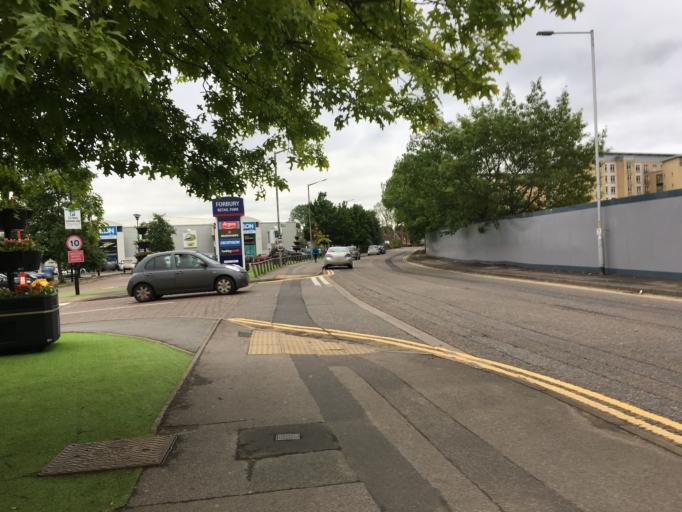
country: GB
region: England
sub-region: Reading
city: Reading
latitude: 51.4574
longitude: -0.9611
